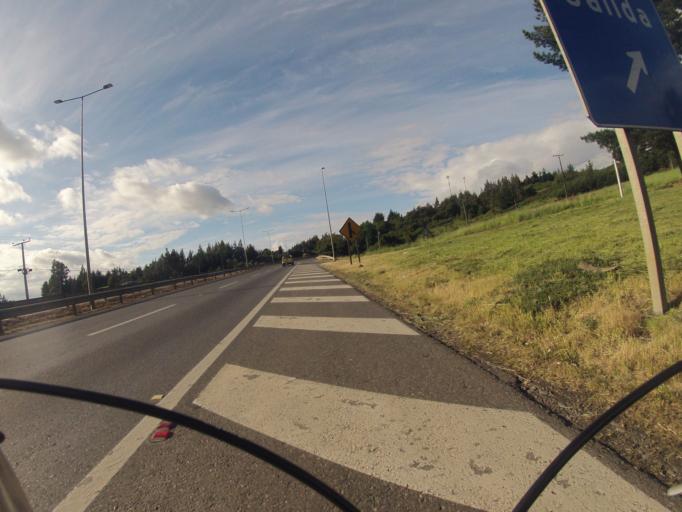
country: CL
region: Araucania
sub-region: Provincia de Cautin
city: Temuco
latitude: -38.8078
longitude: -72.6266
